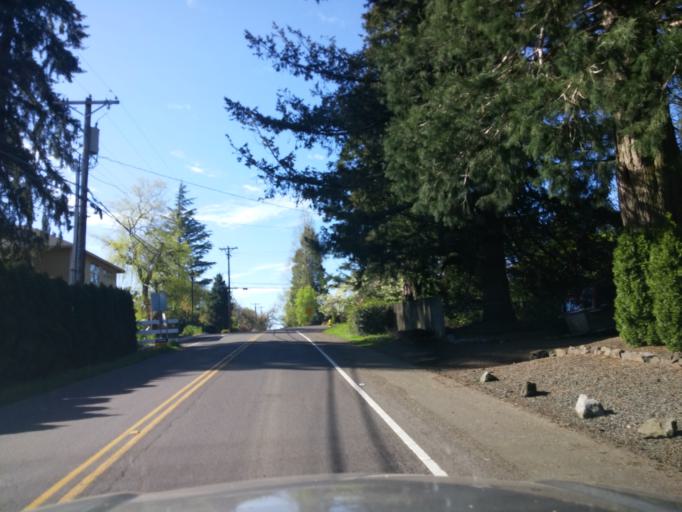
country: US
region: Oregon
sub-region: Washington County
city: Cedar Mill
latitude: 45.5368
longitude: -122.7906
